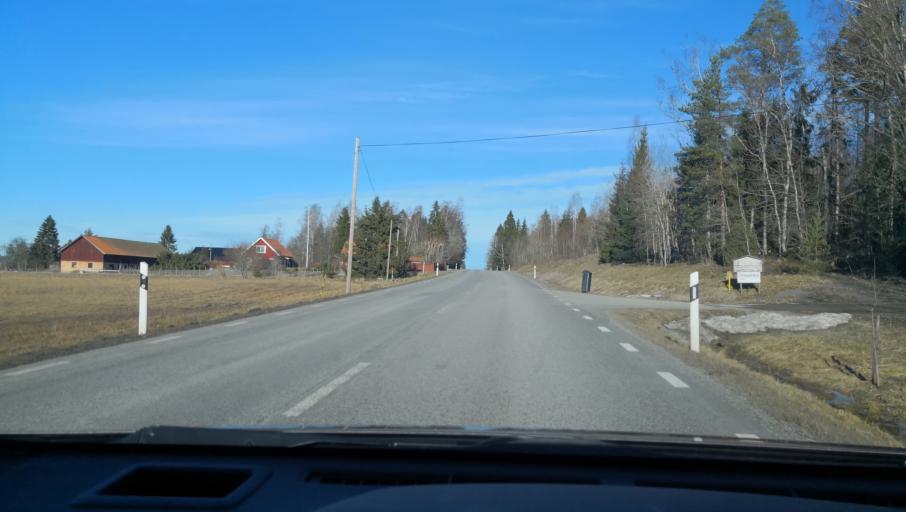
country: SE
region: Uppsala
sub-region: Uppsala Kommun
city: Vattholma
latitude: 60.0635
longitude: 17.7563
